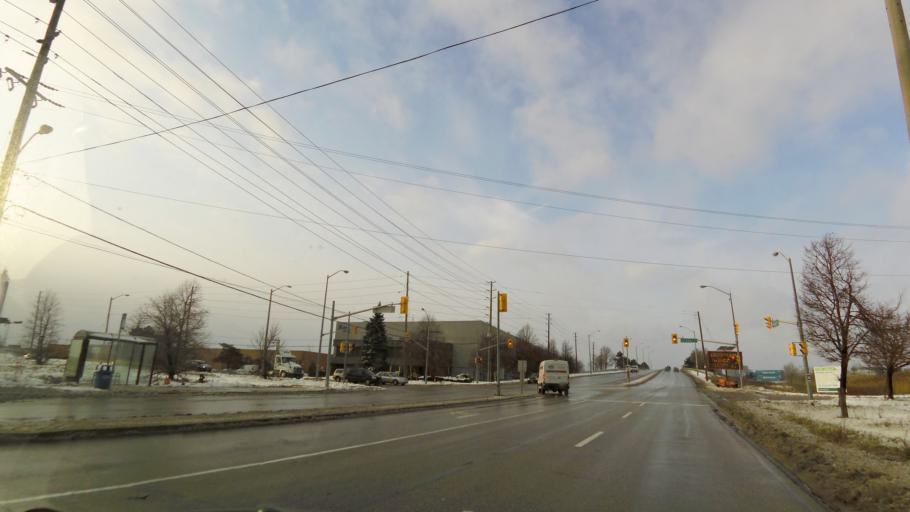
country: CA
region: Ontario
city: Brampton
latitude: 43.6948
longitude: -79.7124
